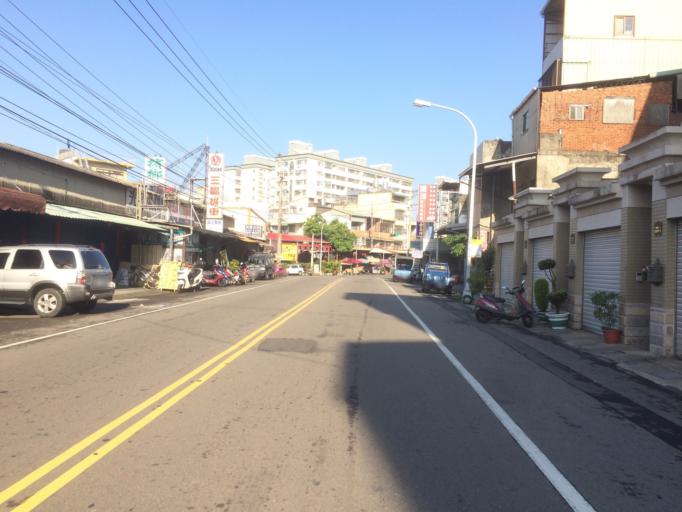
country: TW
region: Taiwan
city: Fengyuan
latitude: 24.2075
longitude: 120.7107
